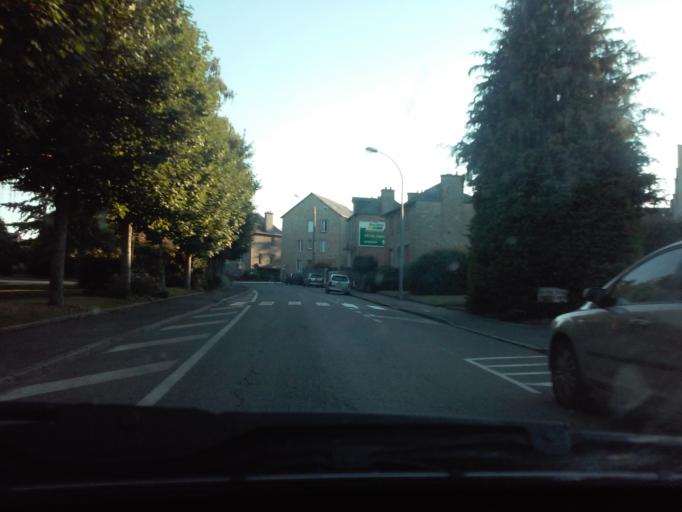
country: FR
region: Brittany
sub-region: Departement des Cotes-d'Armor
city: Lehon
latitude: 48.4600
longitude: -2.0489
